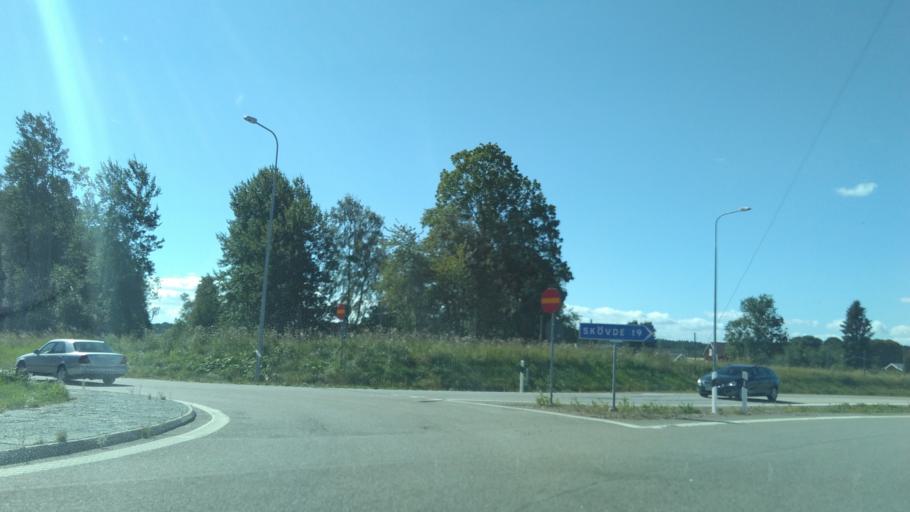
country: SE
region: Vaestra Goetaland
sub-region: Skara Kommun
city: Axvall
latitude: 58.3960
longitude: 13.5625
